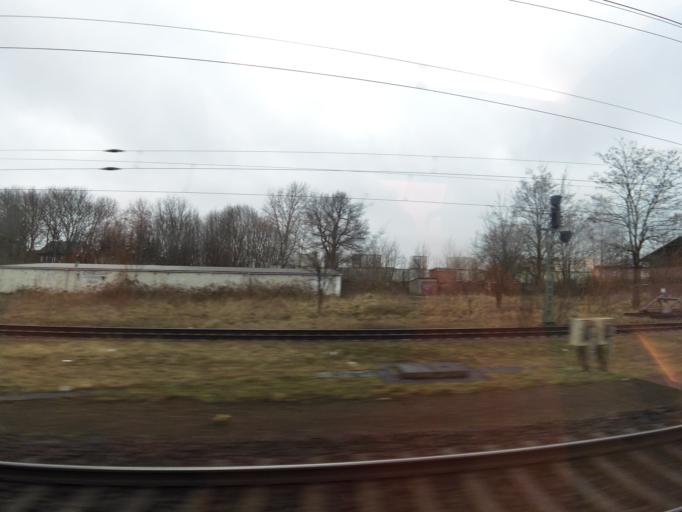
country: DE
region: Saxony-Anhalt
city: Eilsleben
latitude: 52.1496
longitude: 11.2137
